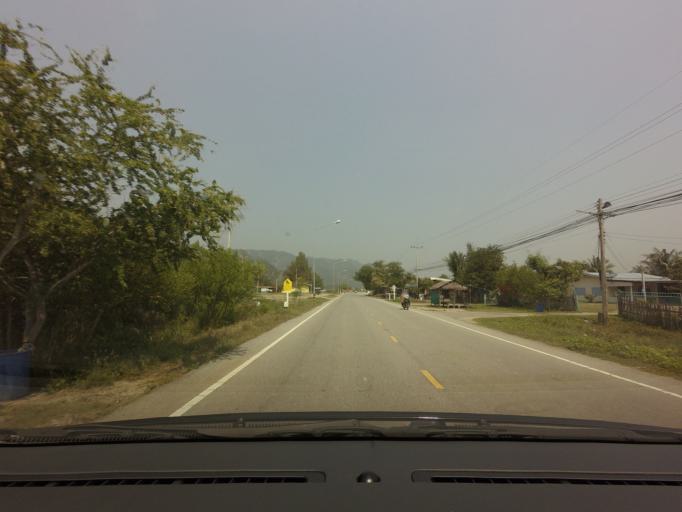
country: TH
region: Prachuap Khiri Khan
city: Kui Buri
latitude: 12.1377
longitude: 99.9638
